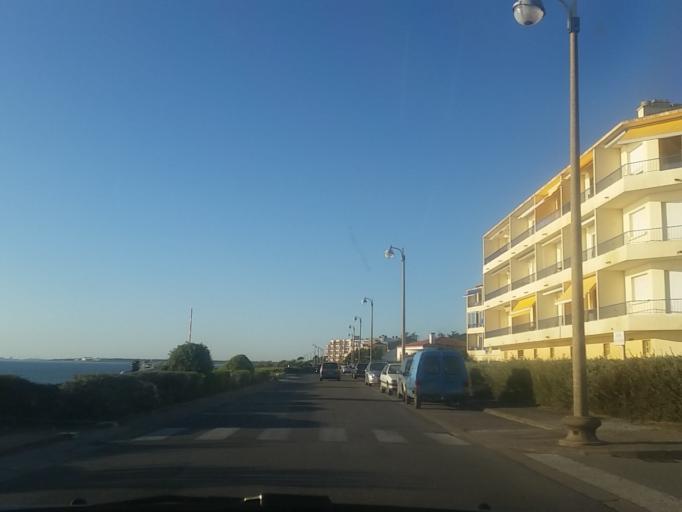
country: FR
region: Pays de la Loire
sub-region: Departement de la Loire-Atlantique
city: Saint-Michel-Chef-Chef
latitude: 47.1751
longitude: -2.1640
